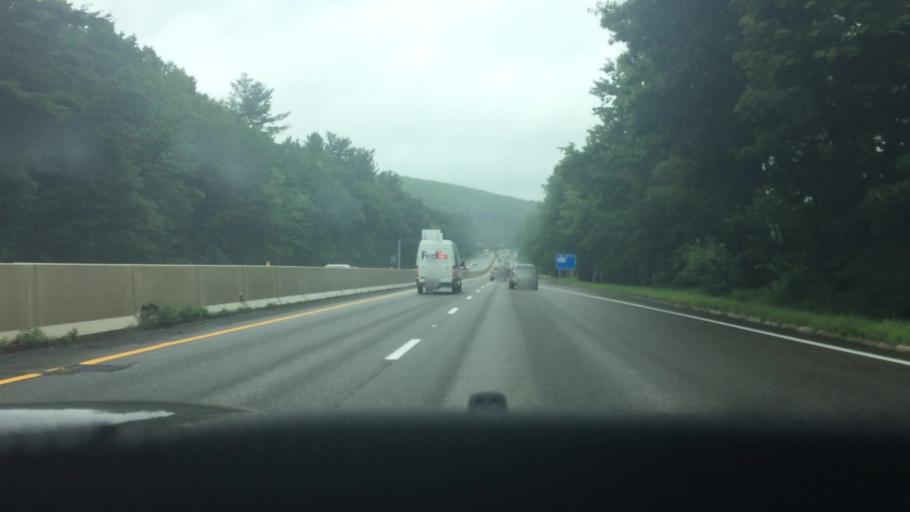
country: US
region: Massachusetts
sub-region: Worcester County
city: Leominster
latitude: 42.5521
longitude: -71.7762
